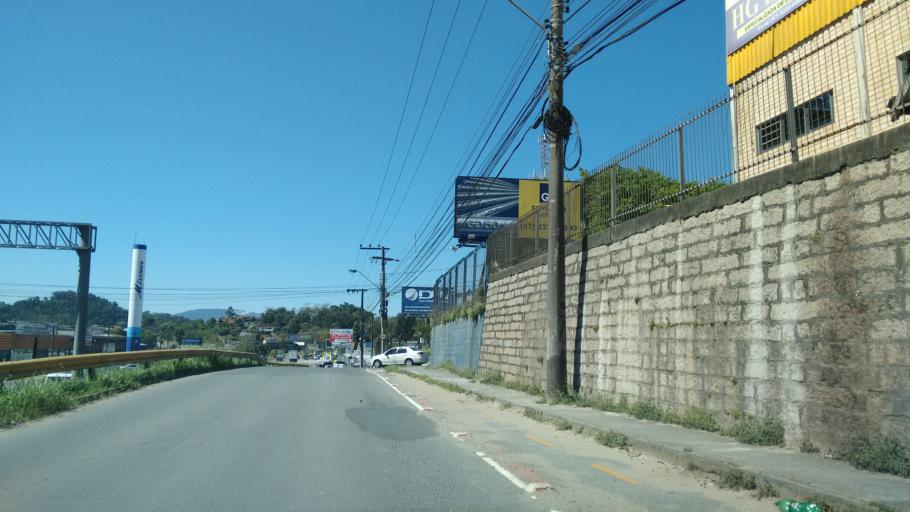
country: BR
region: Santa Catarina
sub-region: Blumenau
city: Blumenau
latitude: -26.8759
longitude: -49.1185
